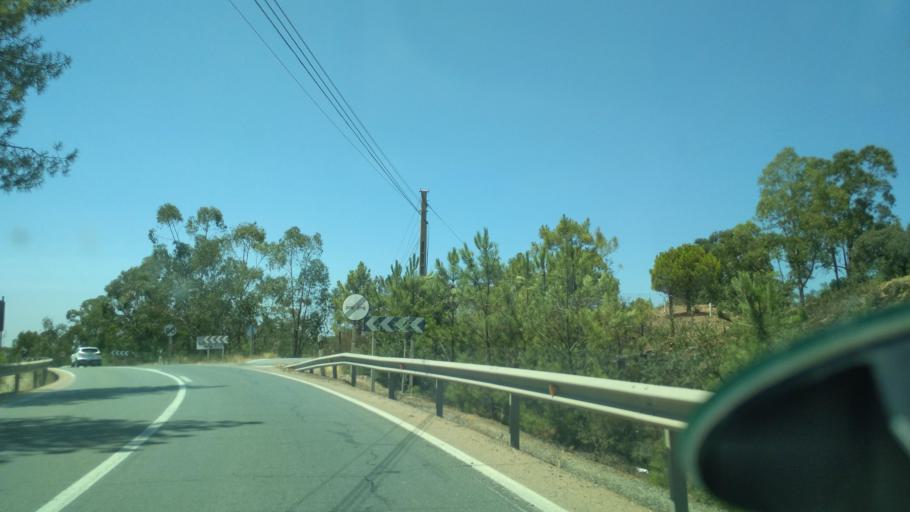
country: ES
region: Andalusia
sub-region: Provincia de Huelva
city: Zalamea la Real
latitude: 37.6921
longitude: -6.6386
